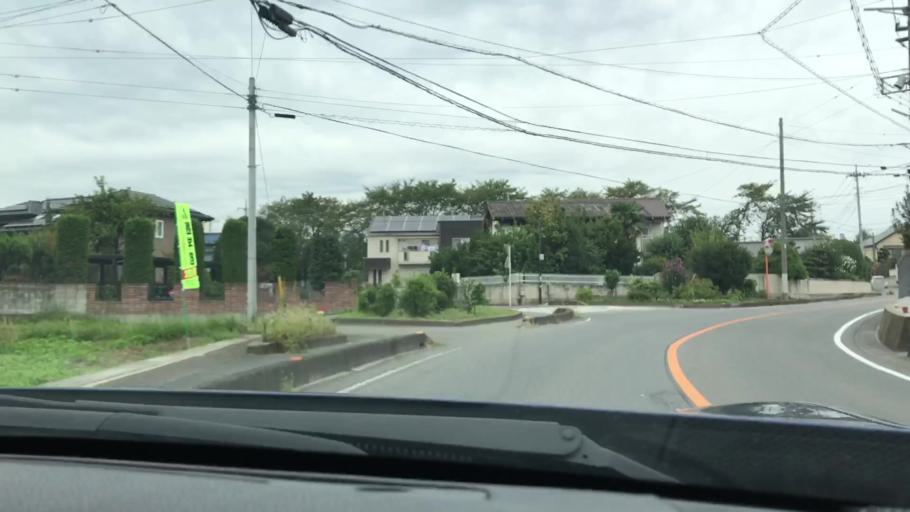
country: JP
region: Gunma
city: Kanekomachi
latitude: 36.3958
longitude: 138.9934
